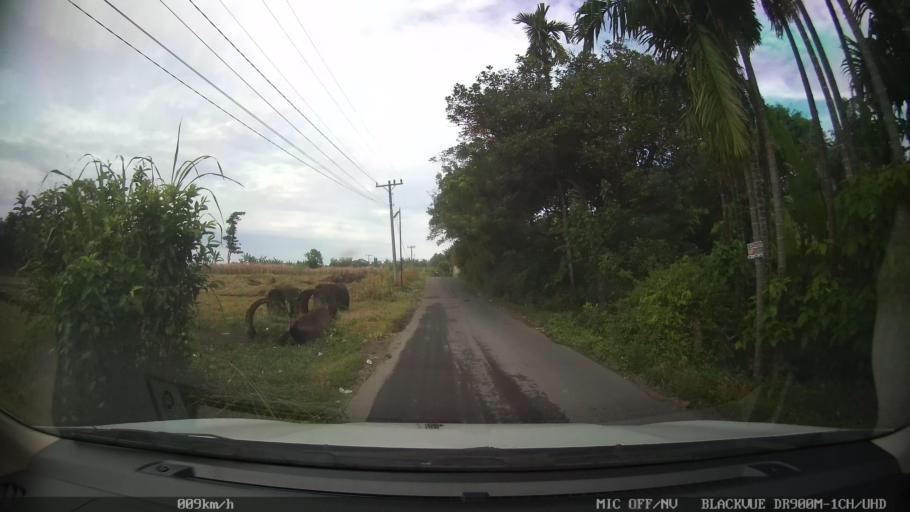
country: ID
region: North Sumatra
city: Sunggal
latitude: 3.5730
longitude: 98.5823
